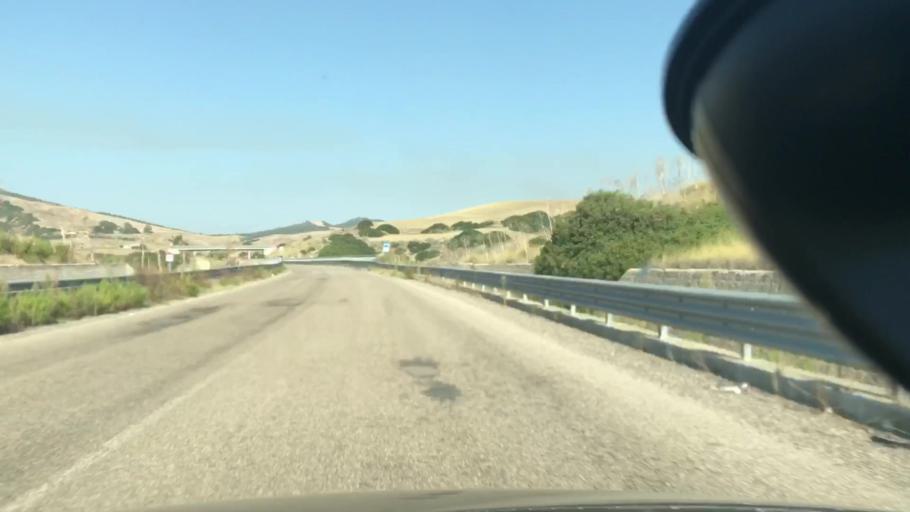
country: IT
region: Basilicate
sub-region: Provincia di Matera
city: La Martella
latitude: 40.6899
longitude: 16.4452
